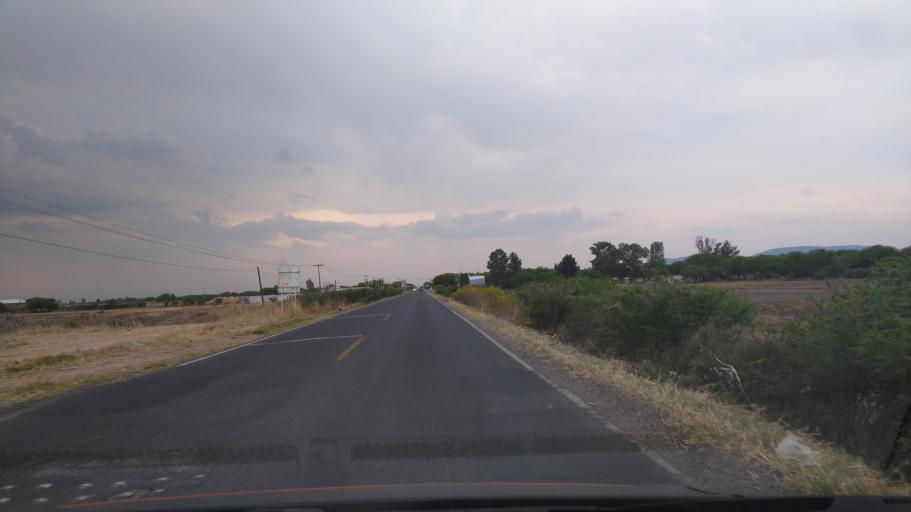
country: MX
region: Guanajuato
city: Ciudad Manuel Doblado
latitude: 20.7475
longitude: -101.9266
